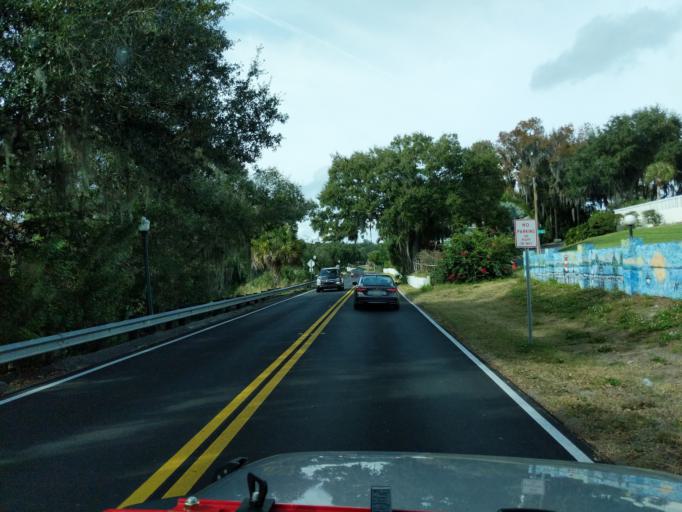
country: US
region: Florida
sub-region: Lake County
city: Mount Dora
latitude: 28.8011
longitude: -81.6475
